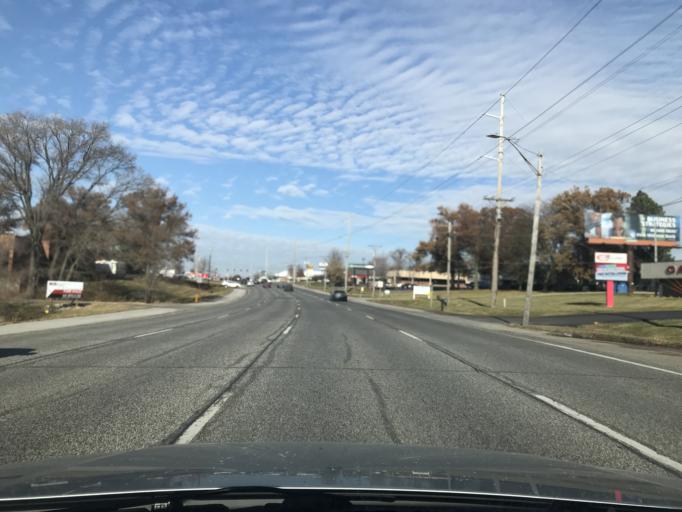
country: US
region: Iowa
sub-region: Scott County
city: Davenport
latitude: 41.5650
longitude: -90.5676
